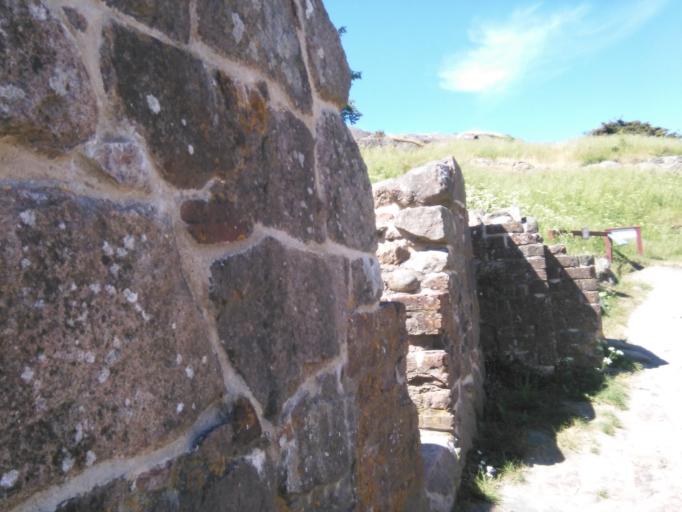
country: DK
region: Capital Region
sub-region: Bornholm Kommune
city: Ronne
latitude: 55.2718
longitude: 14.7570
